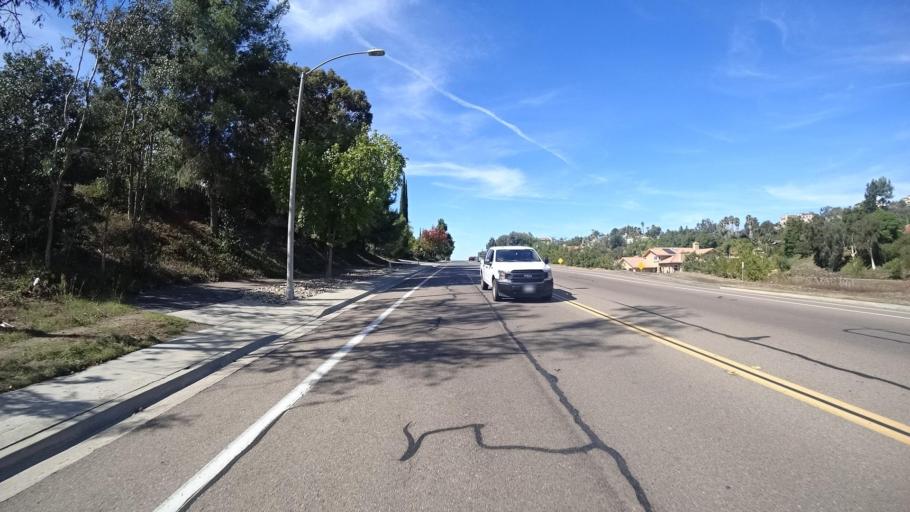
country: US
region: California
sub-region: San Diego County
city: Rancho San Diego
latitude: 32.7513
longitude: -116.9475
